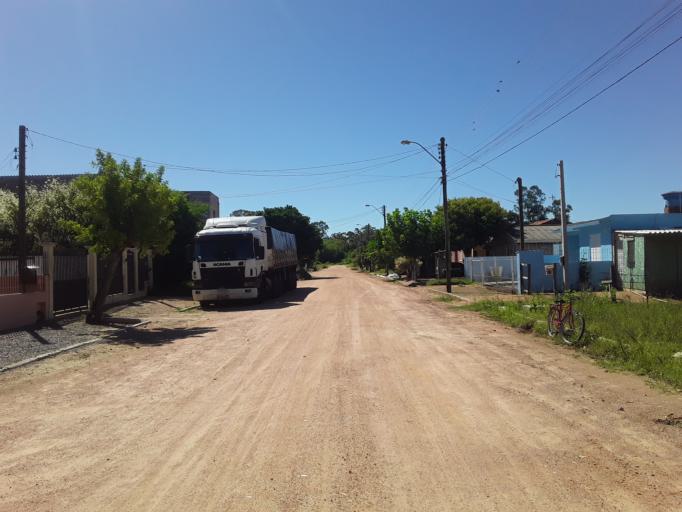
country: BR
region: Rio Grande do Sul
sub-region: Sao Lourenco Do Sul
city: Sao Lourenco do Sul
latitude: -31.3447
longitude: -51.9927
